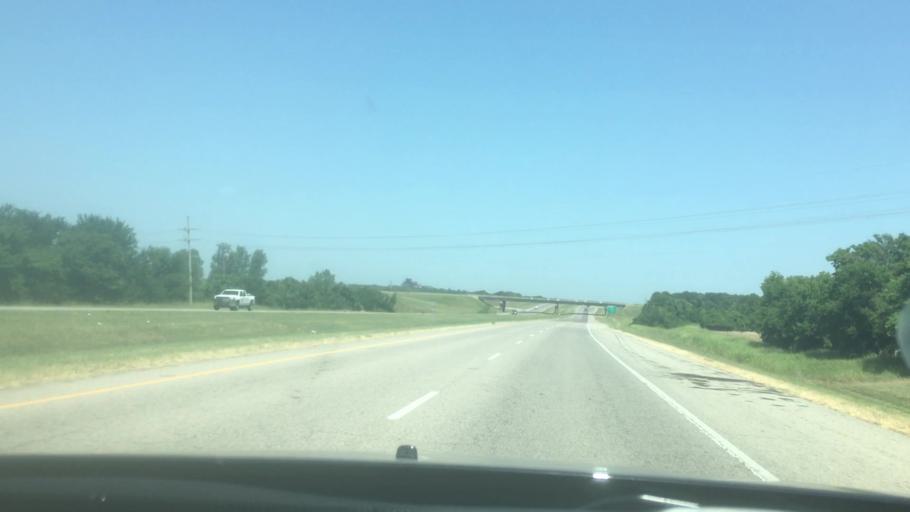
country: US
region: Oklahoma
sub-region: Pontotoc County
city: Ada
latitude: 34.7229
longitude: -96.6309
